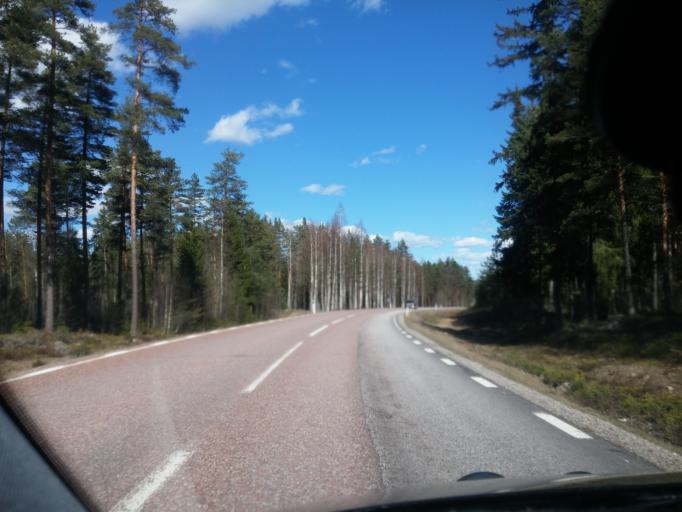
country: SE
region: Dalarna
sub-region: Faluns Kommun
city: Falun
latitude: 60.6940
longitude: 15.7276
